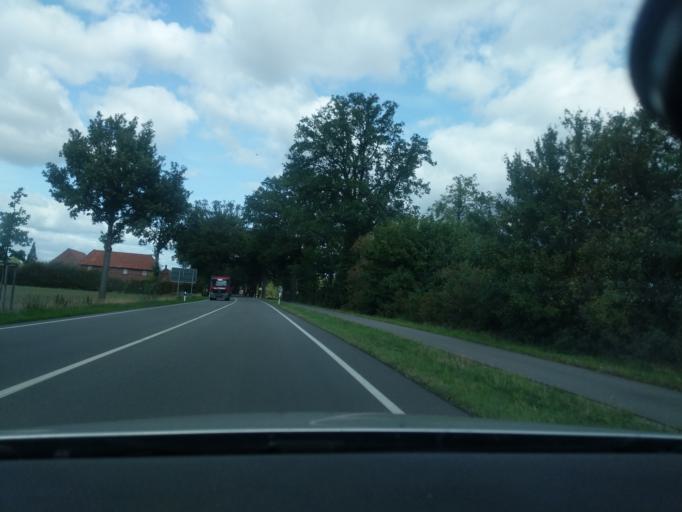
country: DE
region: Lower Saxony
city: Bohmte
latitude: 52.3822
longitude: 8.3110
